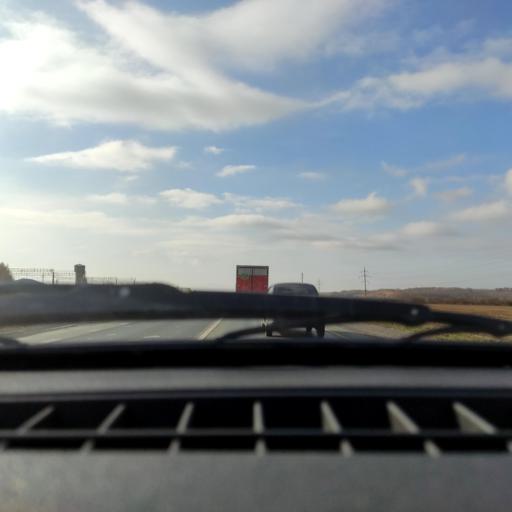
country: RU
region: Bashkortostan
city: Kabakovo
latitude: 54.7087
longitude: 56.2239
